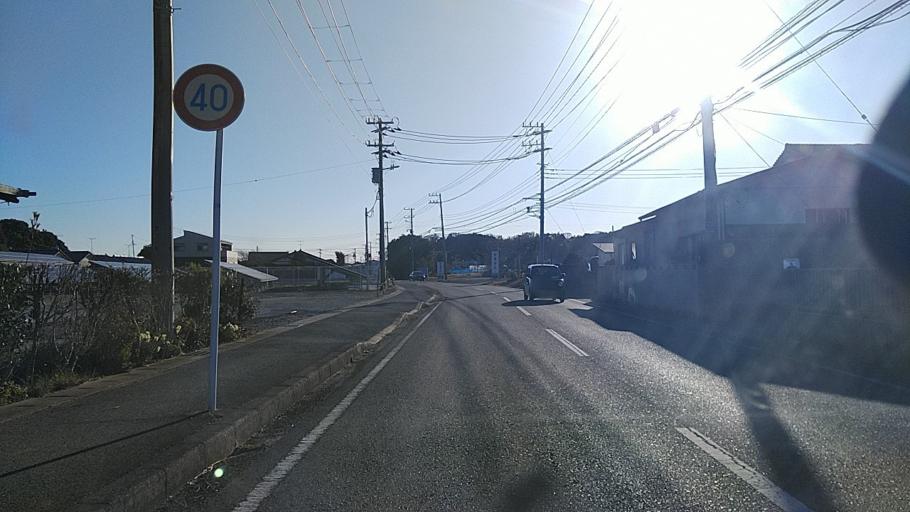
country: JP
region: Chiba
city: Kimitsu
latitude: 35.3200
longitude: 139.8855
